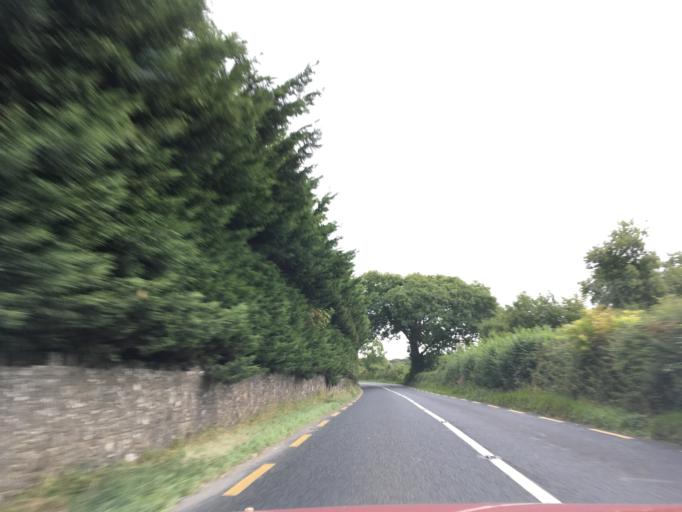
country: IE
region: Munster
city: Cashel
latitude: 52.4443
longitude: -7.8032
